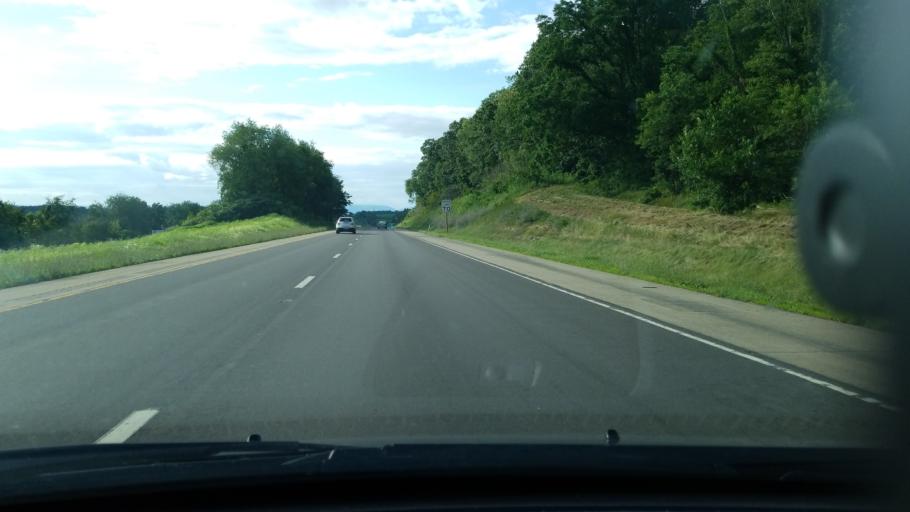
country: US
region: Pennsylvania
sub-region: Northumberland County
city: Milton
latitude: 41.0298
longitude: -76.8041
